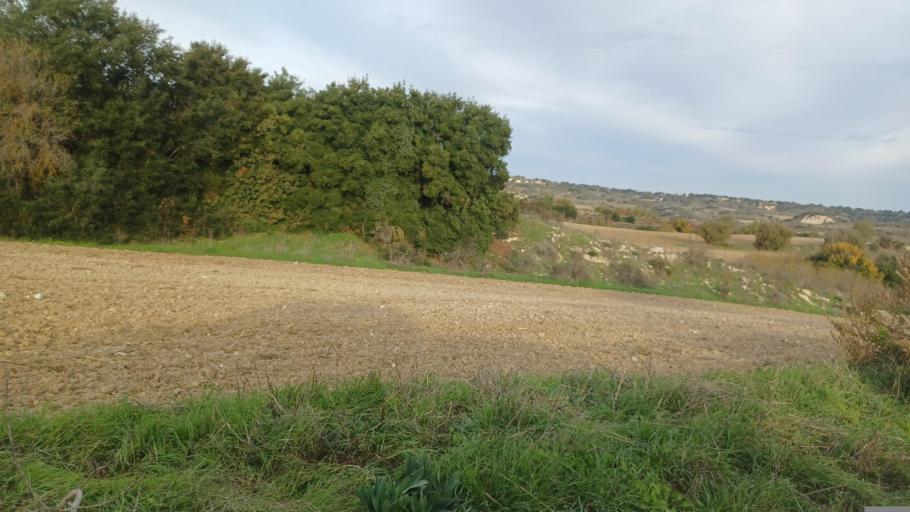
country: CY
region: Pafos
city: Mesogi
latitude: 34.8656
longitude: 32.5195
